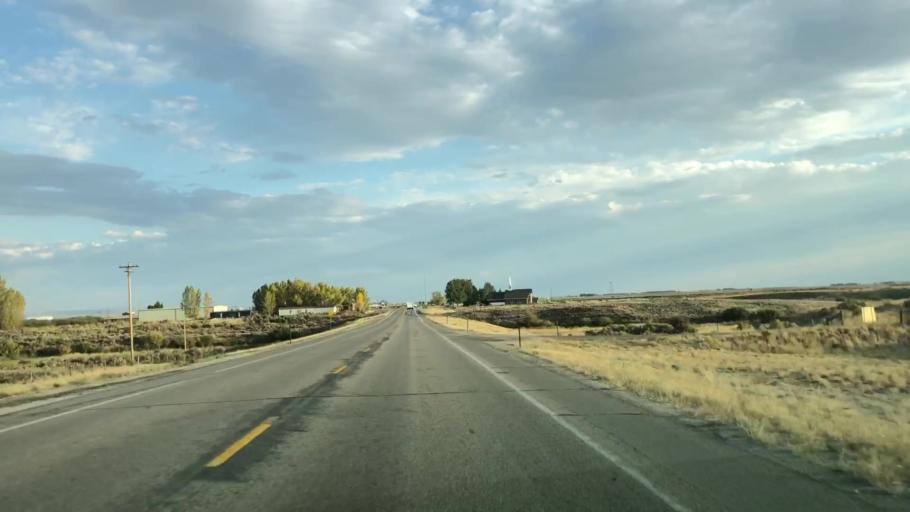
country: US
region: Wyoming
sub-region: Sweetwater County
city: North Rock Springs
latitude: 42.1157
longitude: -109.4513
